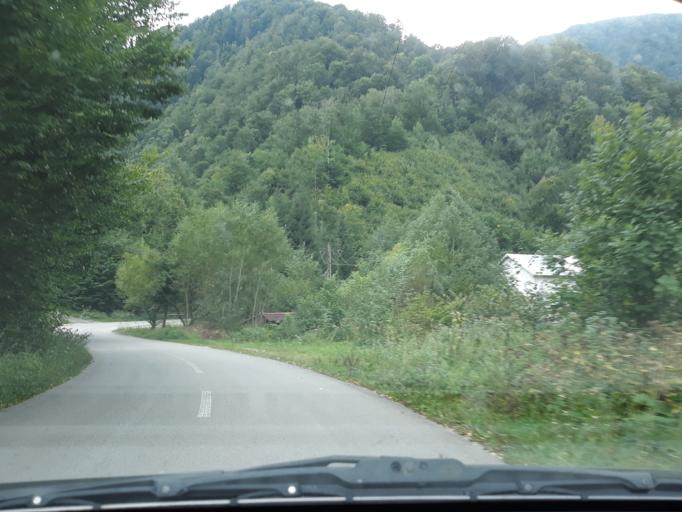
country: RO
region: Bihor
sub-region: Comuna Pietroasa
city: Pietroasa
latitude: 46.5903
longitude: 22.6319
